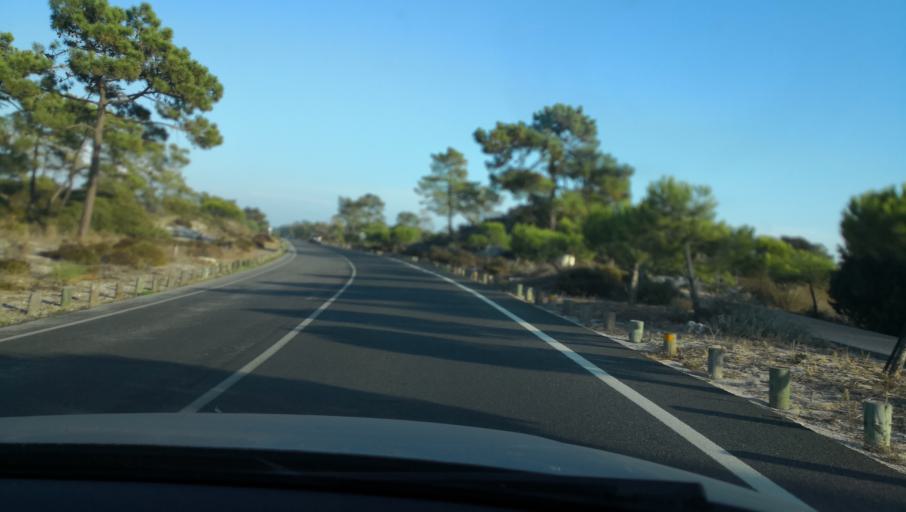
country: PT
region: Setubal
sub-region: Setubal
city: Setubal
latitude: 38.4692
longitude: -8.8828
